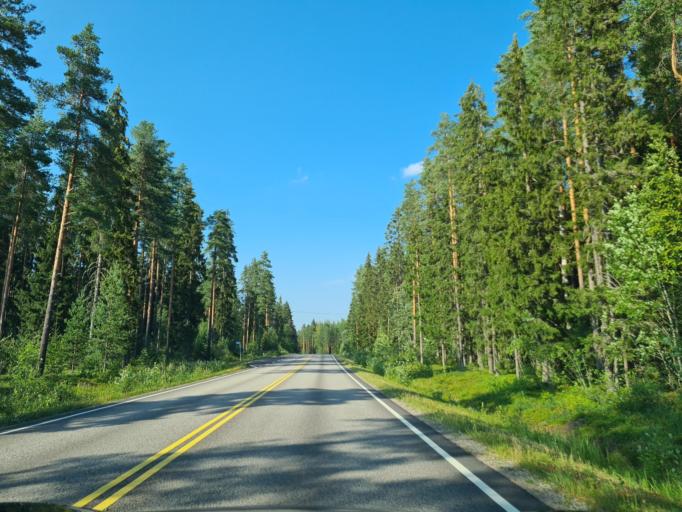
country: FI
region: Satakunta
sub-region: Pohjois-Satakunta
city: Karvia
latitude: 62.2021
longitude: 22.5983
